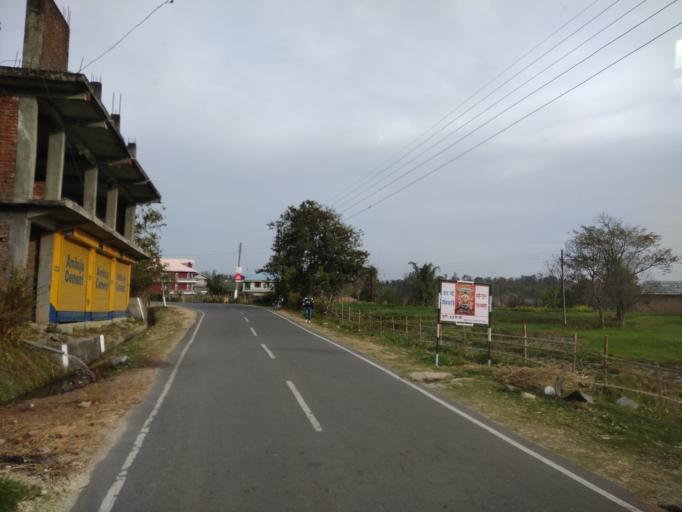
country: IN
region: Himachal Pradesh
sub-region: Kangra
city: Palampur
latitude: 32.1102
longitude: 76.4932
